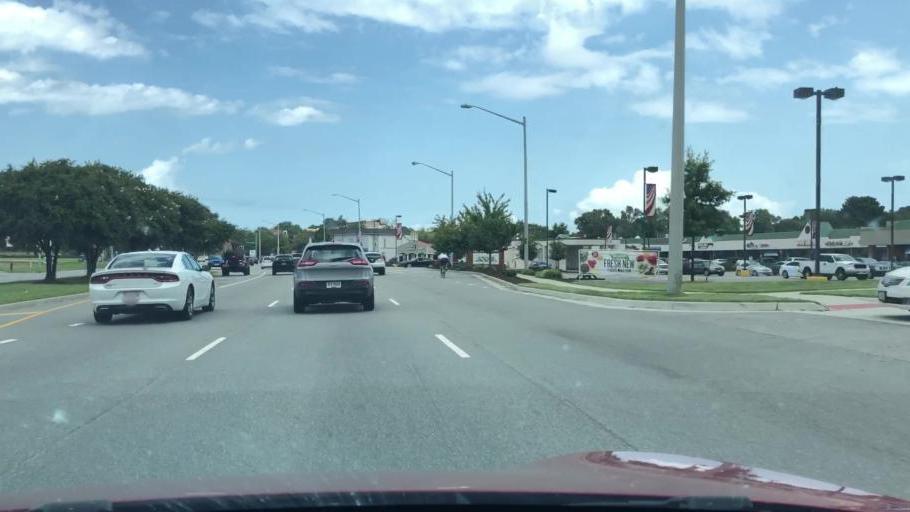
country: US
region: Virginia
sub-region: City of Chesapeake
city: Chesapeake
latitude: 36.8630
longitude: -76.1320
